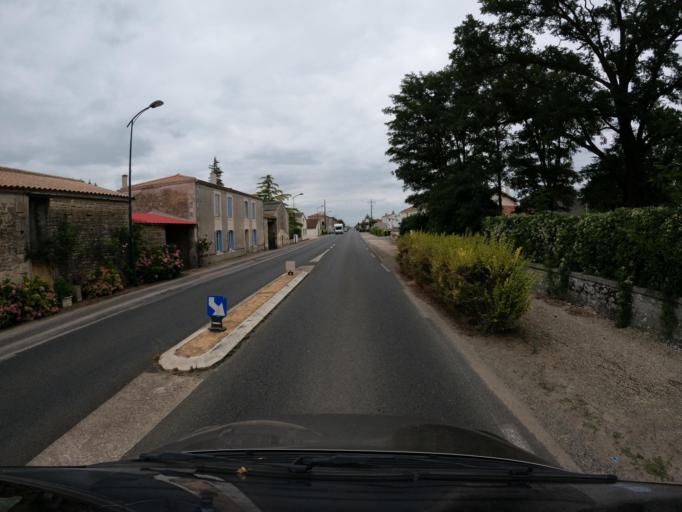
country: FR
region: Pays de la Loire
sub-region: Departement de la Vendee
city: Saint-Hilaire-des-Loges
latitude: 46.4008
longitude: -0.6671
